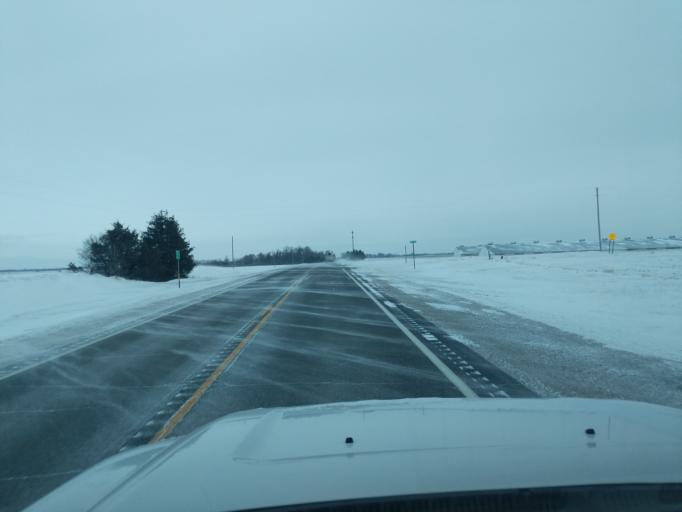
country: US
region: Minnesota
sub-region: Redwood County
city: Redwood Falls
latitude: 44.6079
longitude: -94.9945
